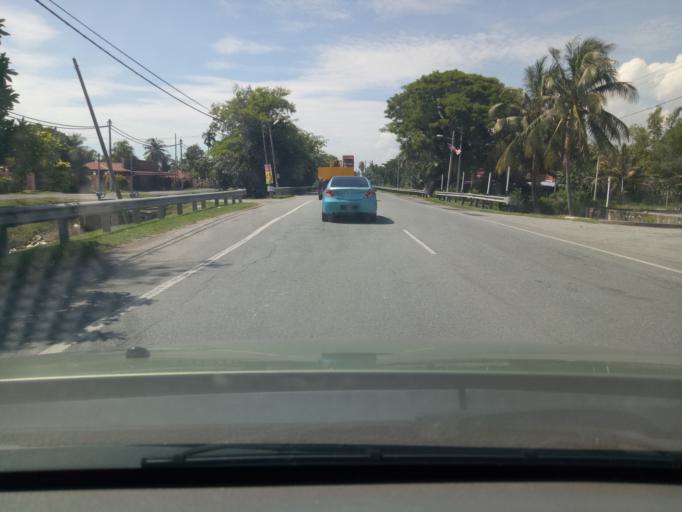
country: MY
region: Kedah
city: Alor Setar
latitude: 5.9682
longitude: 100.4022
